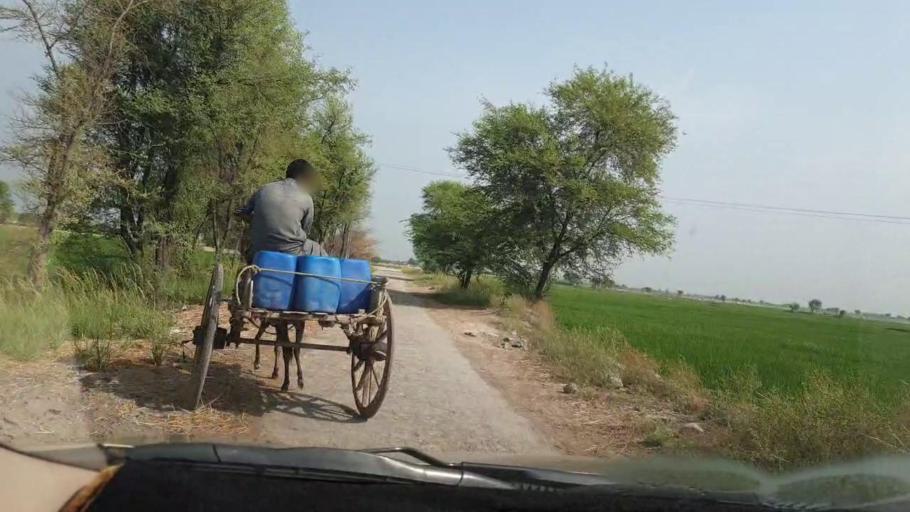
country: PK
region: Sindh
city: Goth Garelo
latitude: 27.4515
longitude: 68.0201
